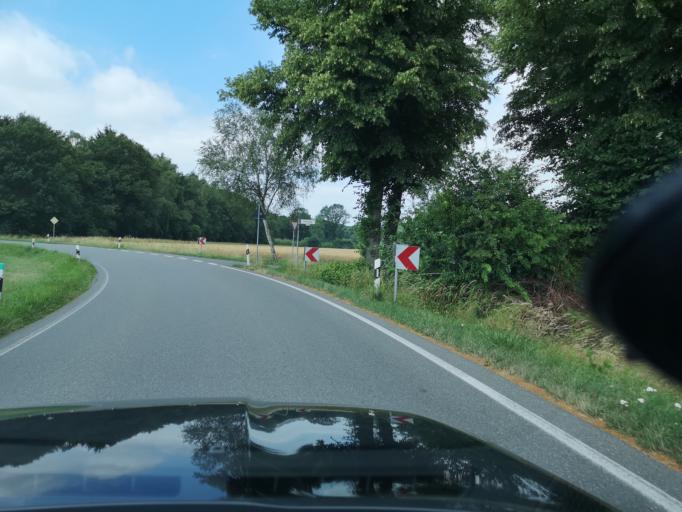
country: DE
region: North Rhine-Westphalia
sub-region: Regierungsbezirk Munster
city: Rhede
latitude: 51.8911
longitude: 6.6812
